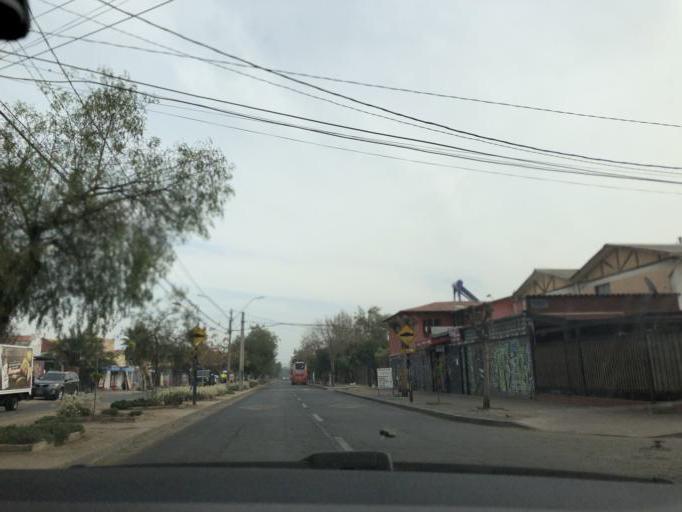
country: CL
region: Santiago Metropolitan
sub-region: Provincia de Cordillera
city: Puente Alto
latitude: -33.5925
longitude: -70.5623
